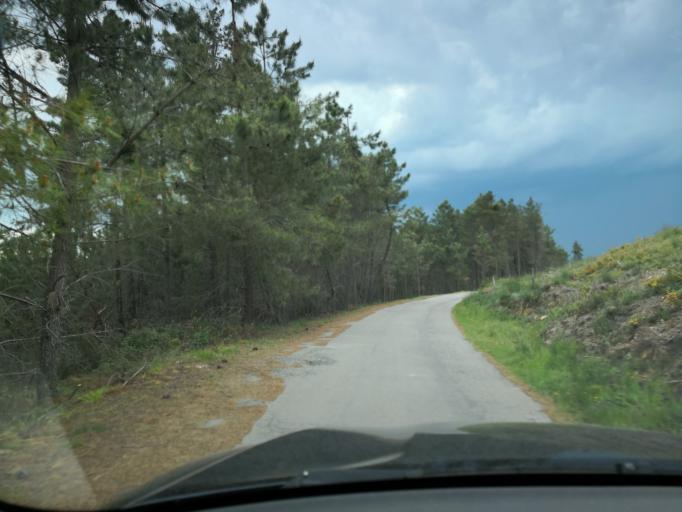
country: PT
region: Vila Real
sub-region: Sabrosa
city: Vilela
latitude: 41.2398
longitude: -7.6692
